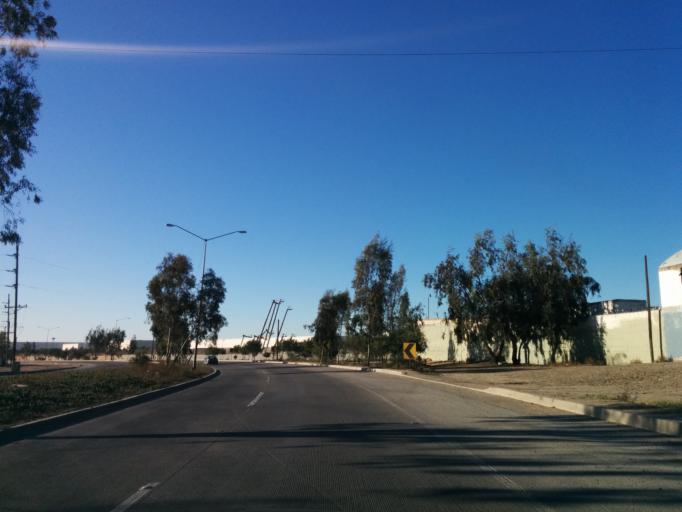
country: MX
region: Baja California
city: Tijuana
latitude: 32.5484
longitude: -116.9494
